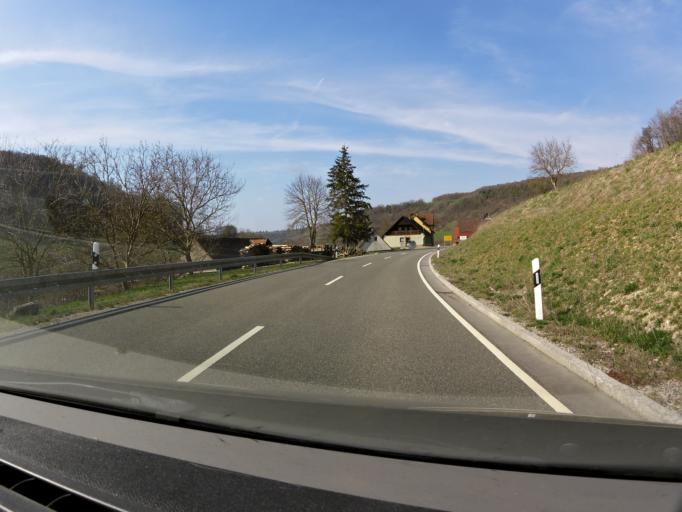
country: DE
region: Bavaria
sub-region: Regierungsbezirk Mittelfranken
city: Adelshofen
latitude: 49.4356
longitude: 10.1408
